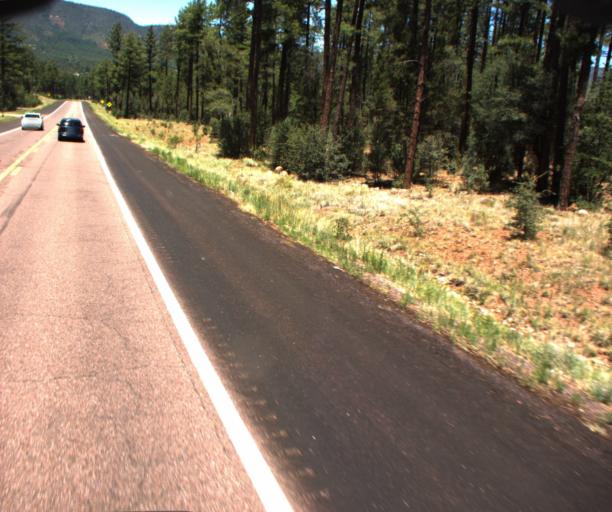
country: US
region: Arizona
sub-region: Gila County
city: Pine
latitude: 34.3686
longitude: -111.4380
